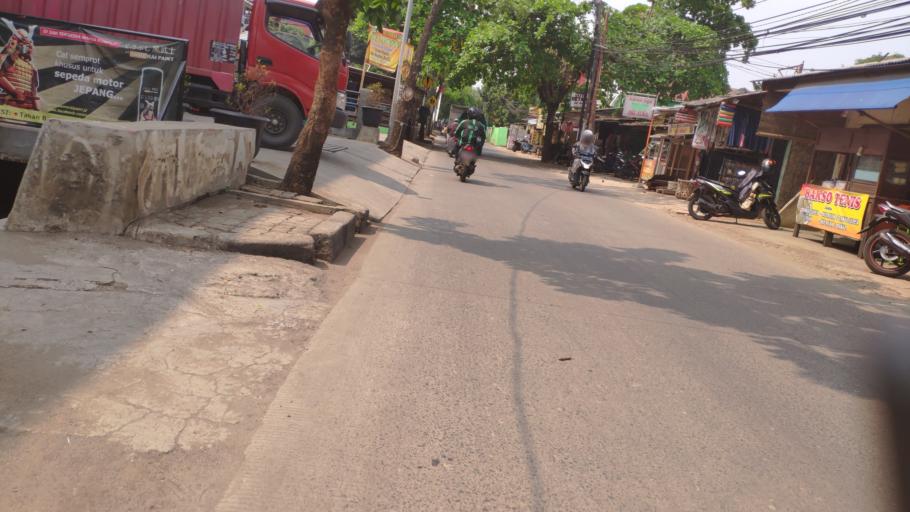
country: ID
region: West Java
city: Sawangan
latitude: -6.3815
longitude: 106.7904
